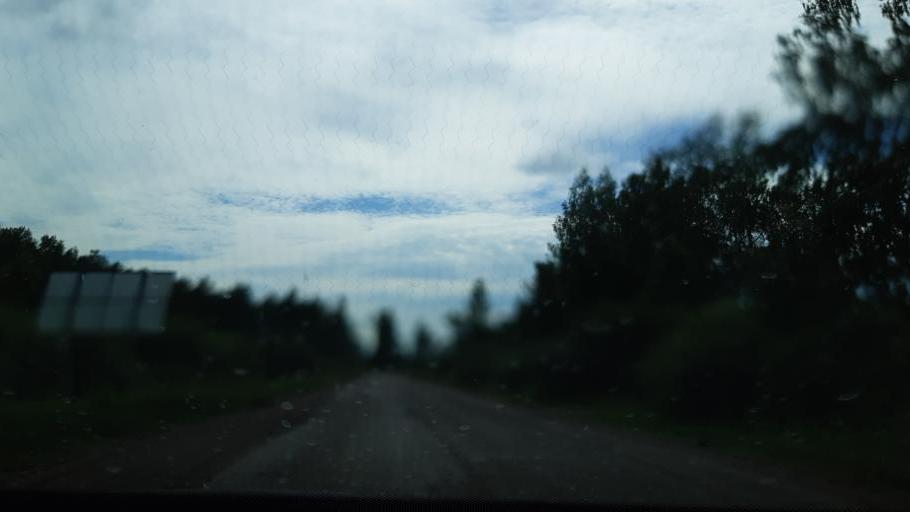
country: RU
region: Moskovskaya
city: Vereya
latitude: 55.3058
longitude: 36.1059
